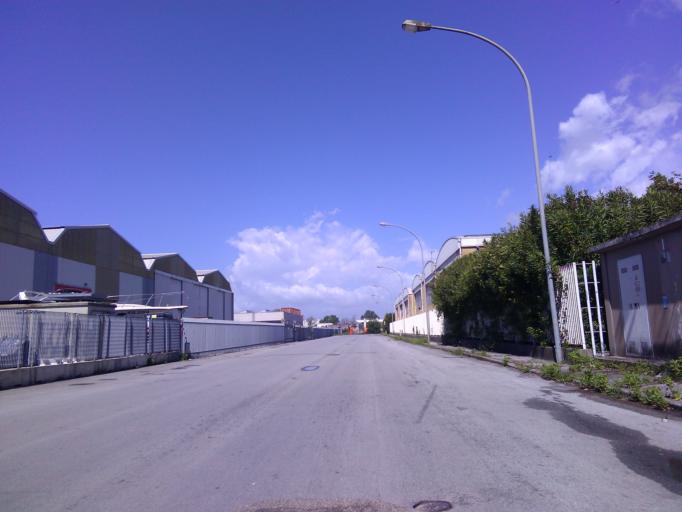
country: IT
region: Tuscany
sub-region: Provincia di Massa-Carrara
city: Massa
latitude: 44.0288
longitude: 10.1025
